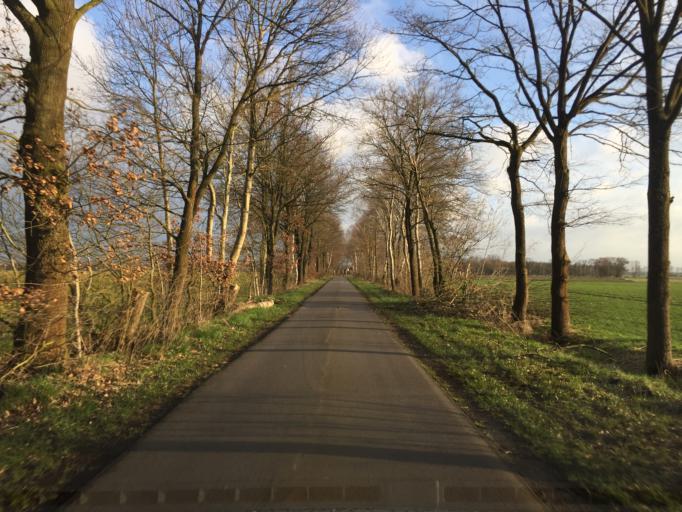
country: DE
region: Lower Saxony
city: Borstel
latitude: 52.6138
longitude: 8.9185
